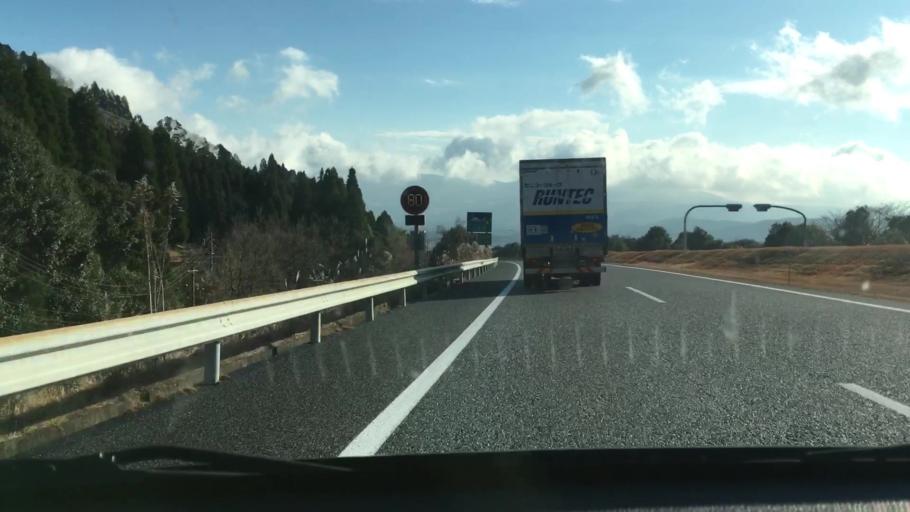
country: JP
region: Kumamoto
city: Hitoyoshi
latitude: 32.0759
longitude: 130.7930
